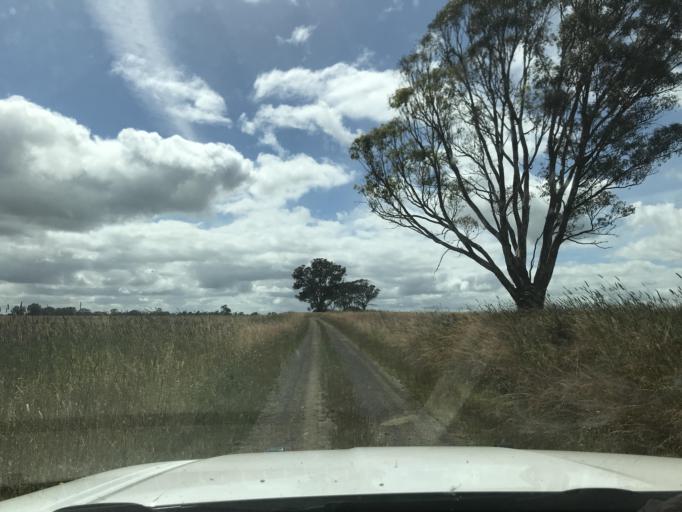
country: AU
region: South Australia
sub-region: Naracoorte and Lucindale
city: Naracoorte
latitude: -37.0088
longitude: 141.0674
